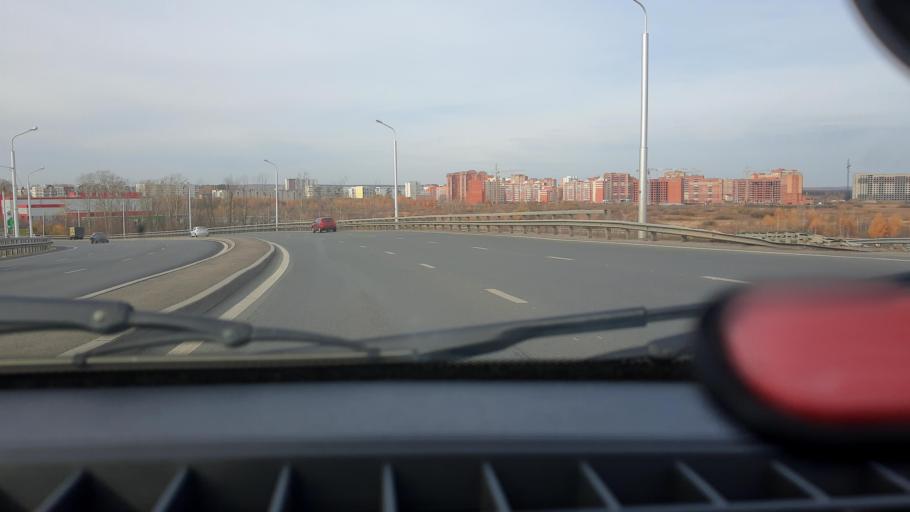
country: RU
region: Bashkortostan
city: Mikhaylovka
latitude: 54.7057
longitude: 55.8560
